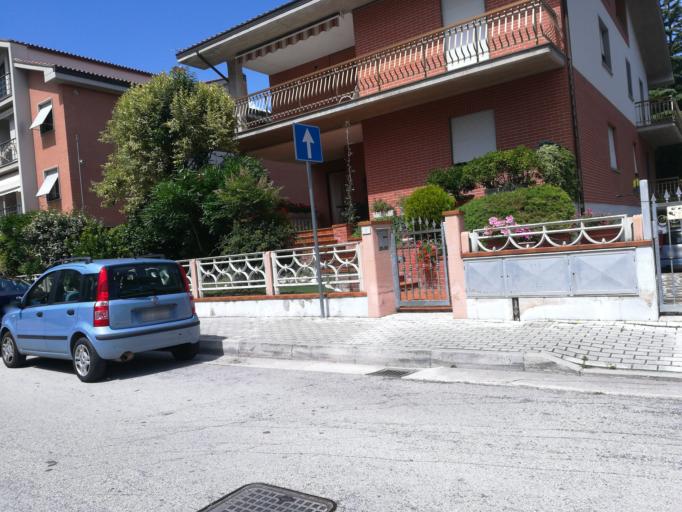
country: IT
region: The Marches
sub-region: Provincia di Macerata
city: Tolentino
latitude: 43.2138
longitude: 13.2924
